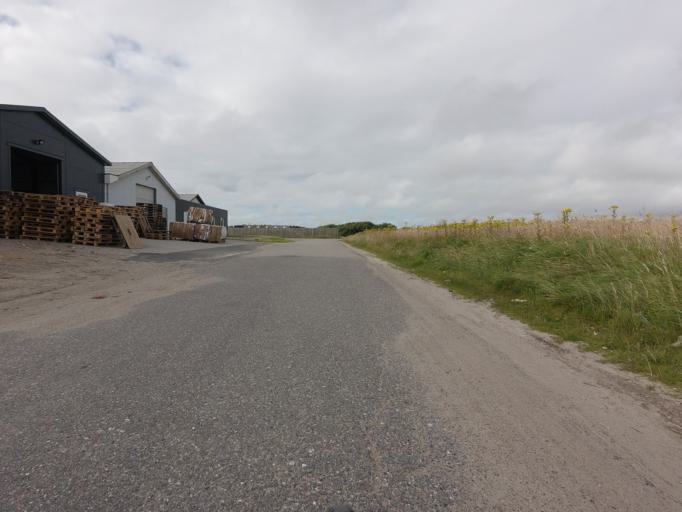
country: DK
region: North Denmark
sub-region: Jammerbugt Kommune
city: Pandrup
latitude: 57.3724
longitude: 9.7311
